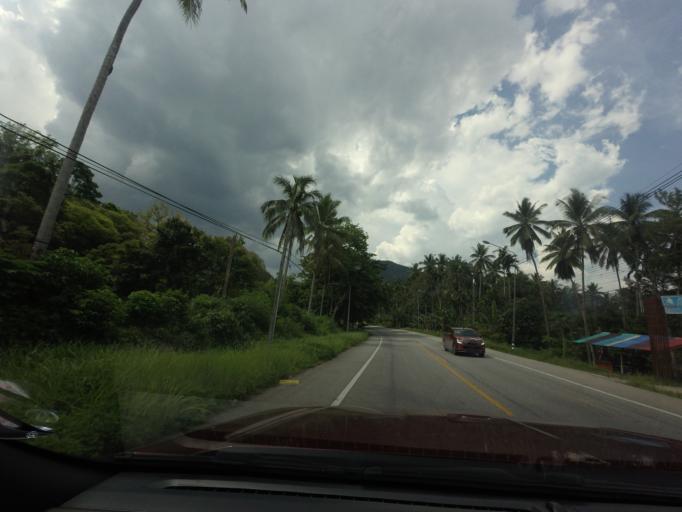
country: TH
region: Yala
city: Than To
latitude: 6.1940
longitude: 101.1734
